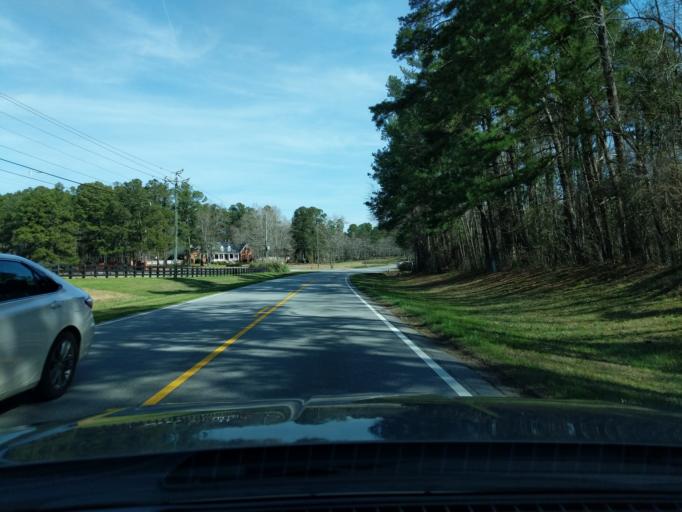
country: US
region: Georgia
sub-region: Columbia County
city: Evans
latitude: 33.5602
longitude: -82.1269
